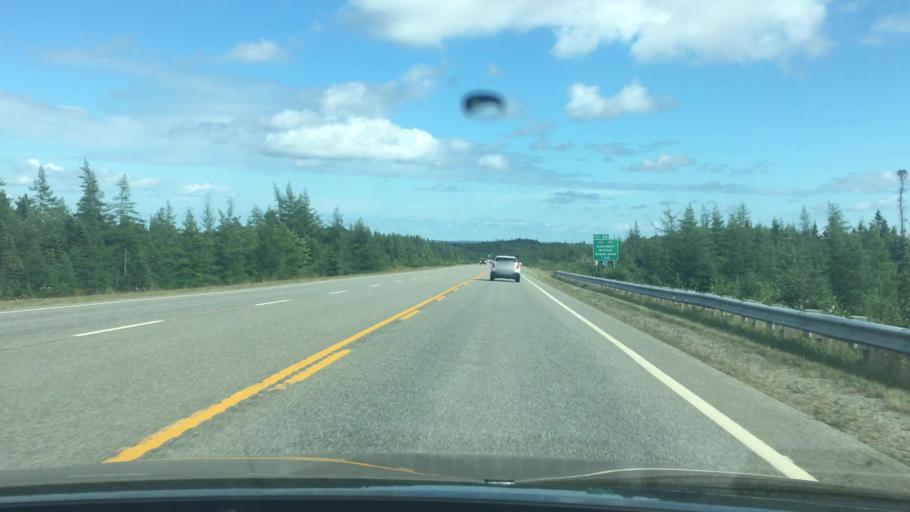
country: CA
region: Nova Scotia
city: Port Hawkesbury
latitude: 45.6187
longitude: -61.1091
